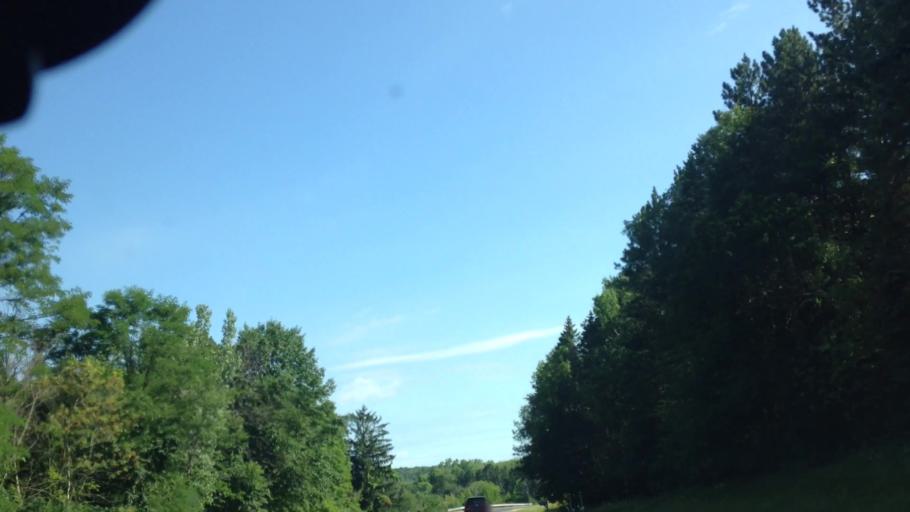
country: US
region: Wisconsin
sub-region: Washington County
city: Slinger
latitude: 43.3720
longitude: -88.2568
